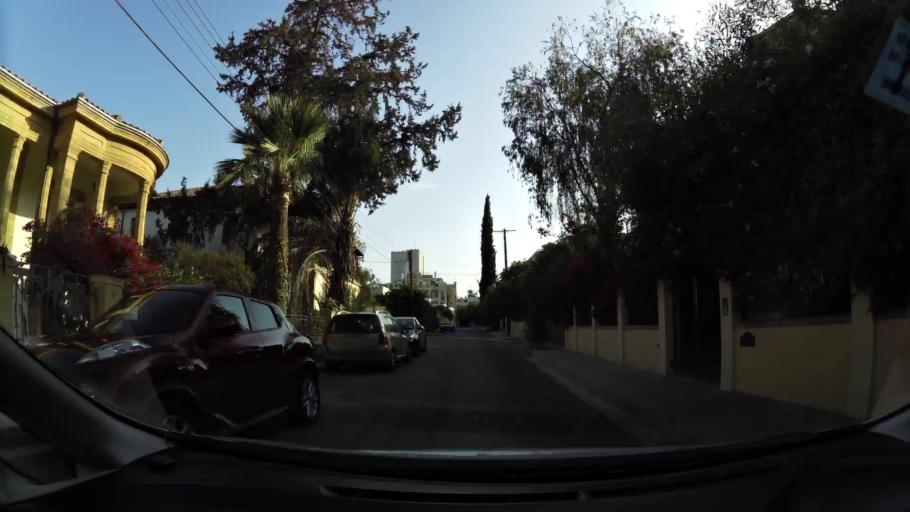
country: CY
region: Lefkosia
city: Nicosia
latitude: 35.1721
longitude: 33.3497
